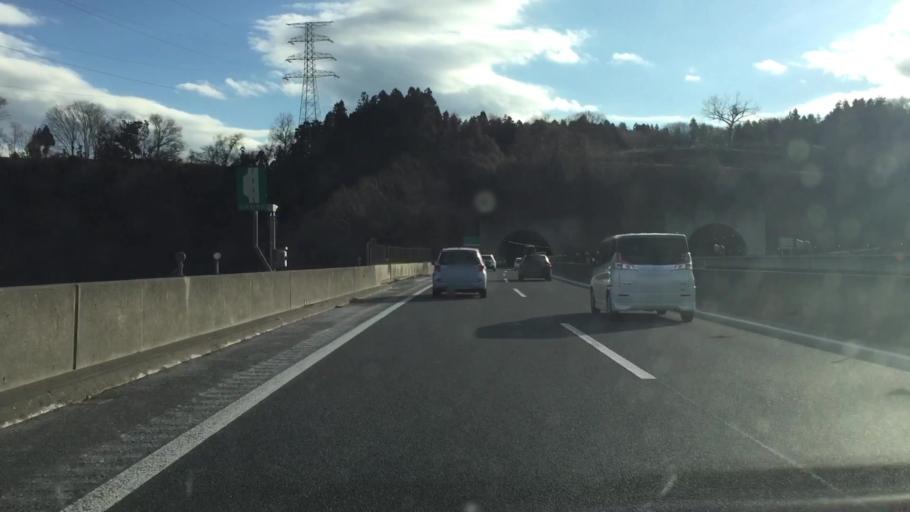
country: JP
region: Gunma
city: Numata
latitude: 36.5877
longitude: 139.0669
